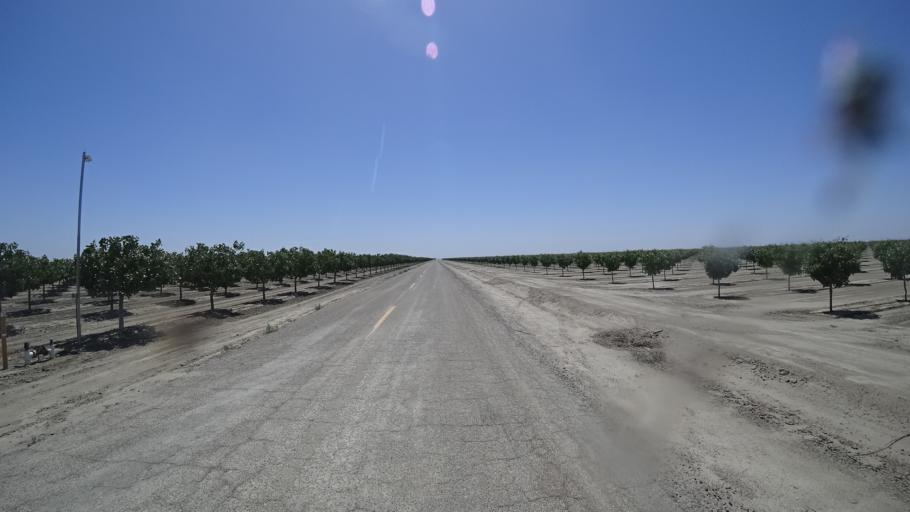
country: US
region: California
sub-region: Kings County
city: Corcoran
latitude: 36.1058
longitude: -119.5989
